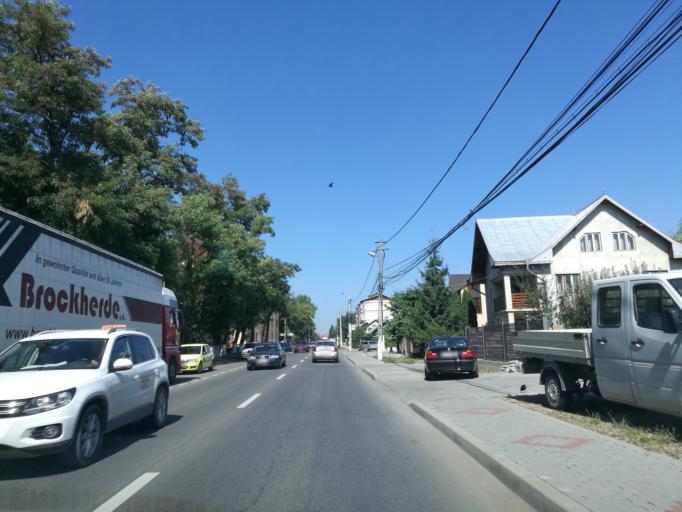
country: RO
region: Suceava
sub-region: Municipiul Suceava
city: Radauti
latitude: 47.8349
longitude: 25.9303
